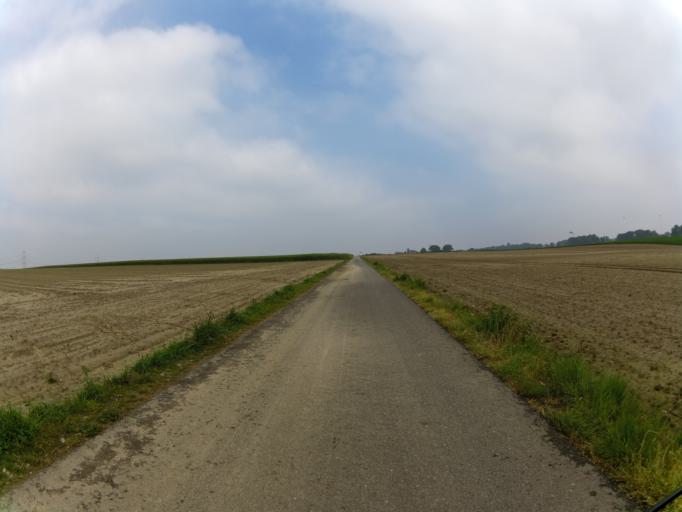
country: DE
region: North Rhine-Westphalia
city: Geilenkirchen
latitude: 51.0127
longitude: 6.1305
